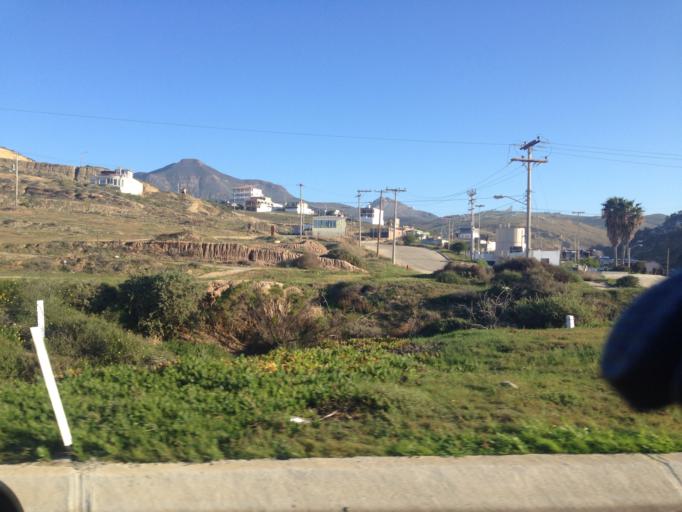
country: MX
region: Baja California
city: Primo Tapia
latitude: 32.2489
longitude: -116.9400
